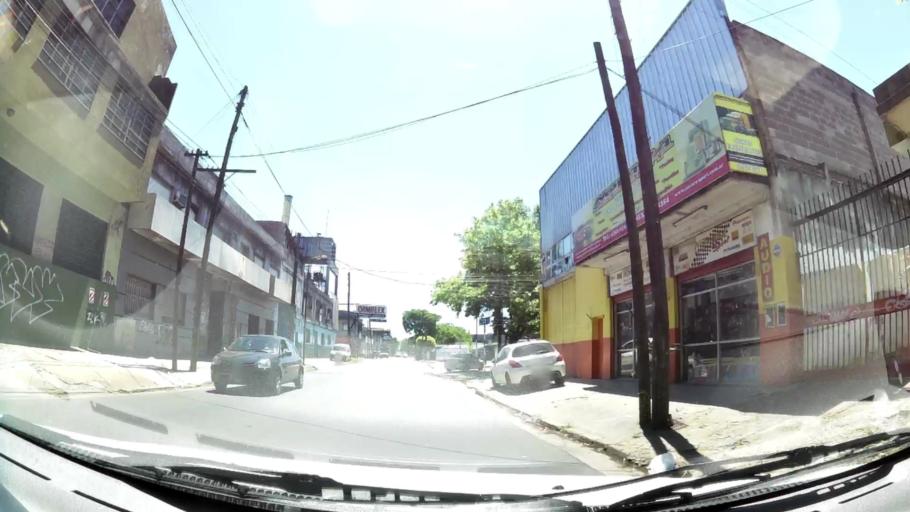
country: AR
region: Buenos Aires
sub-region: Partido de General San Martin
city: General San Martin
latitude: -34.5547
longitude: -58.5322
